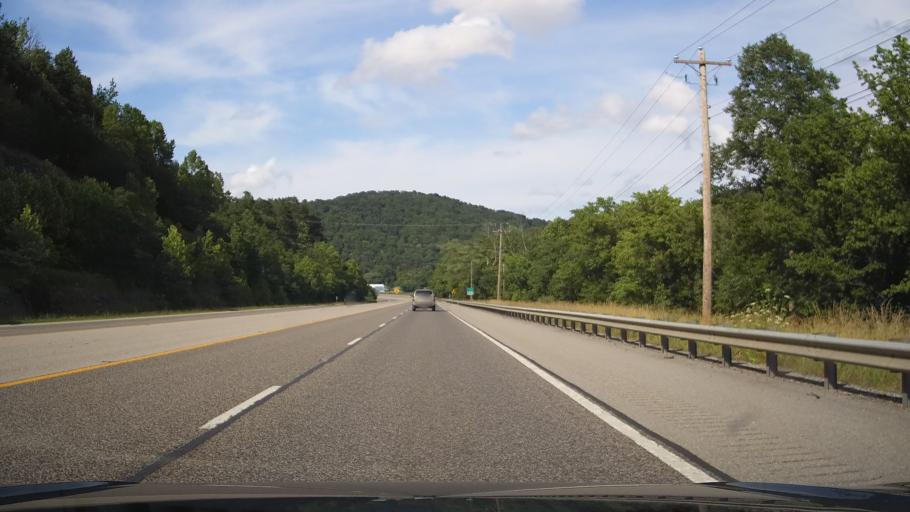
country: US
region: Kentucky
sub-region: Lawrence County
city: Louisa
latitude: 37.9894
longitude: -82.6639
